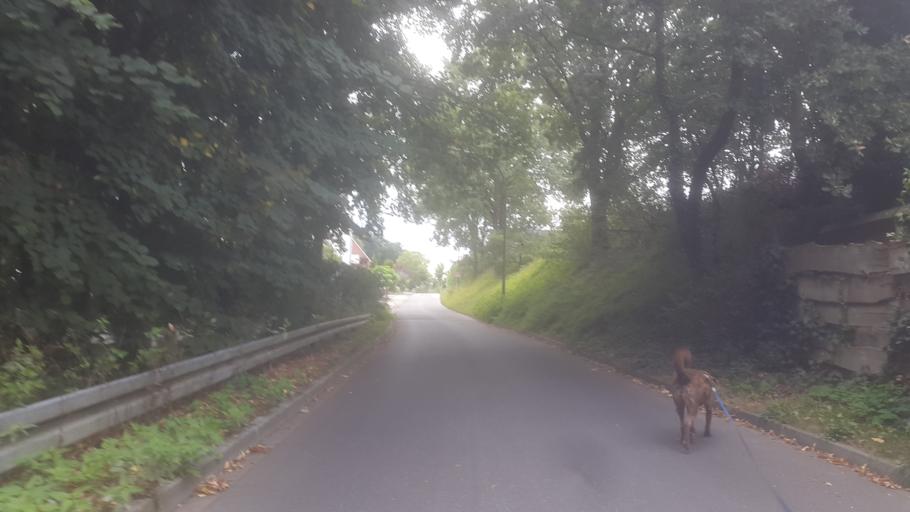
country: DE
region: North Rhine-Westphalia
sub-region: Regierungsbezirk Munster
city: Everswinkel
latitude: 51.9755
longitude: 7.9059
